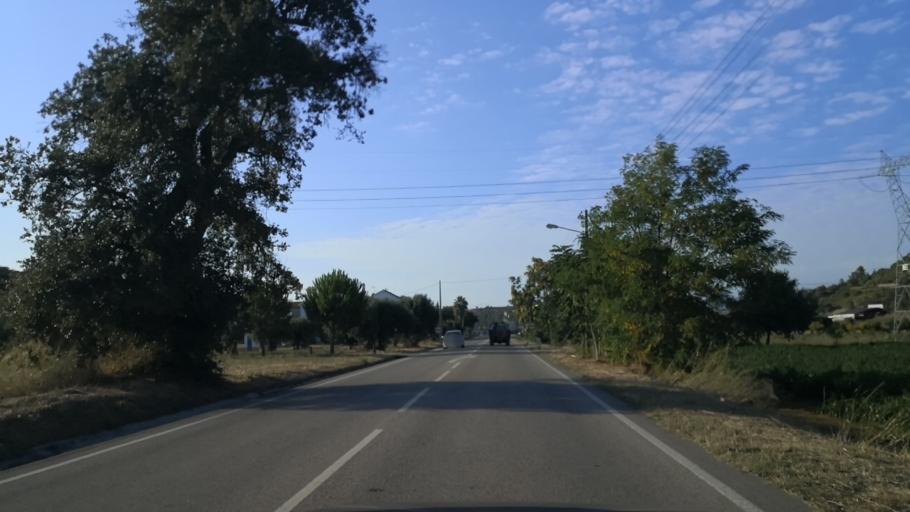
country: PT
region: Santarem
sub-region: Alcanena
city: Alcanena
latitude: 39.3715
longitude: -8.6590
